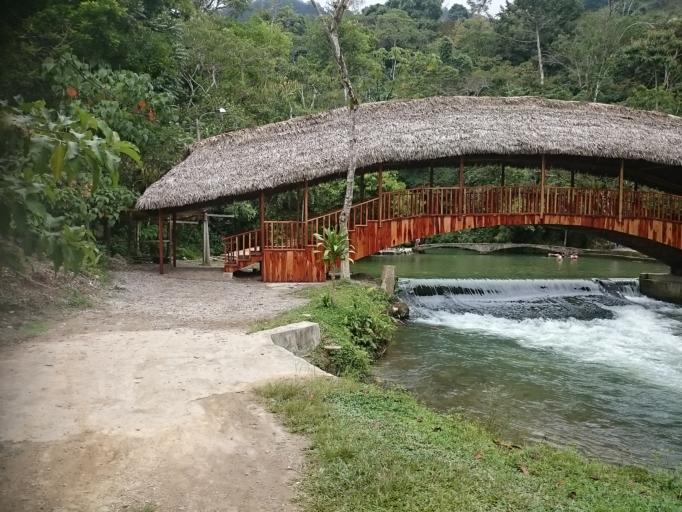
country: PE
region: San Martin
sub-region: Provincia de Rioja
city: Nueva Cajamarca
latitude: -5.9911
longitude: -77.2872
